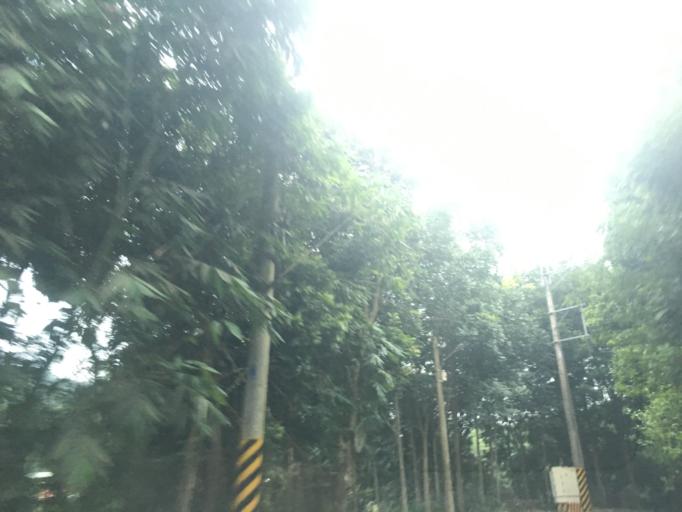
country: TW
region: Taiwan
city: Fengyuan
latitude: 24.1877
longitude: 120.7467
